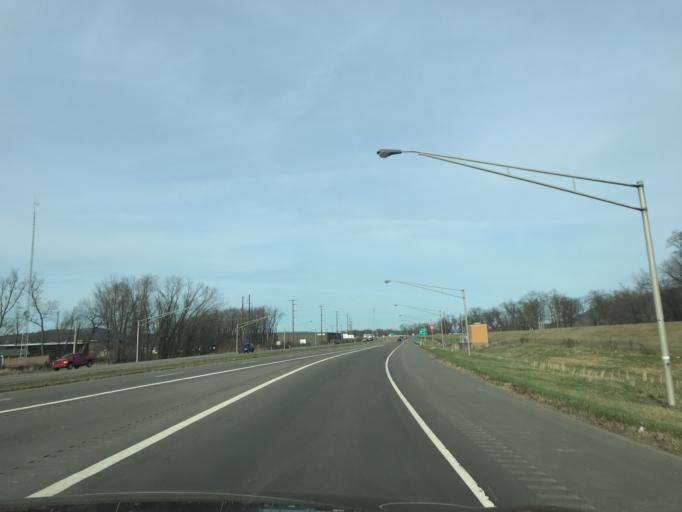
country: US
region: Pennsylvania
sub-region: Lycoming County
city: Duboistown
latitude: 41.2237
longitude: -77.0597
